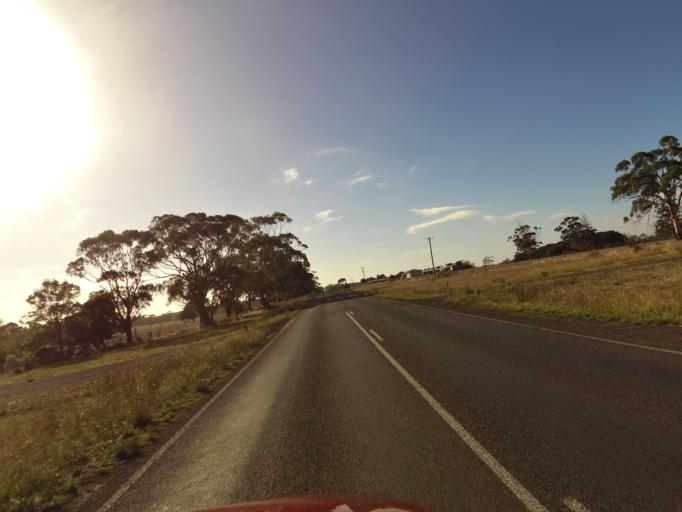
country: AU
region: Victoria
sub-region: Warrnambool
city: Allansford
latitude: -38.3901
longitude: 142.8791
